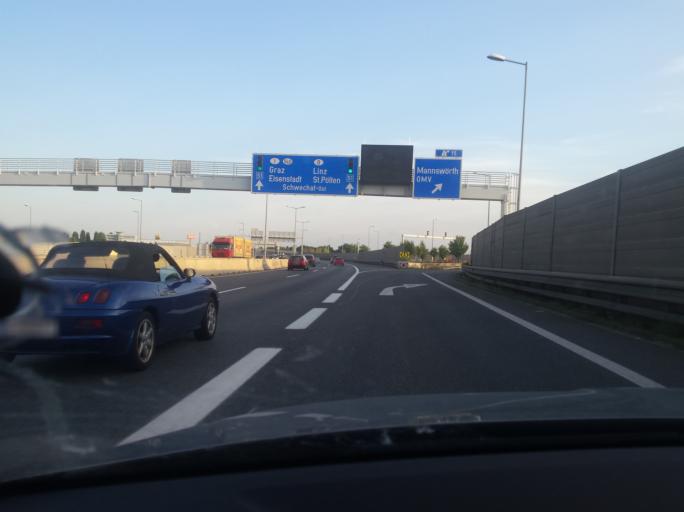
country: AT
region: Lower Austria
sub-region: Politischer Bezirk Wien-Umgebung
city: Schwechat
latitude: 48.1474
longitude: 16.4874
